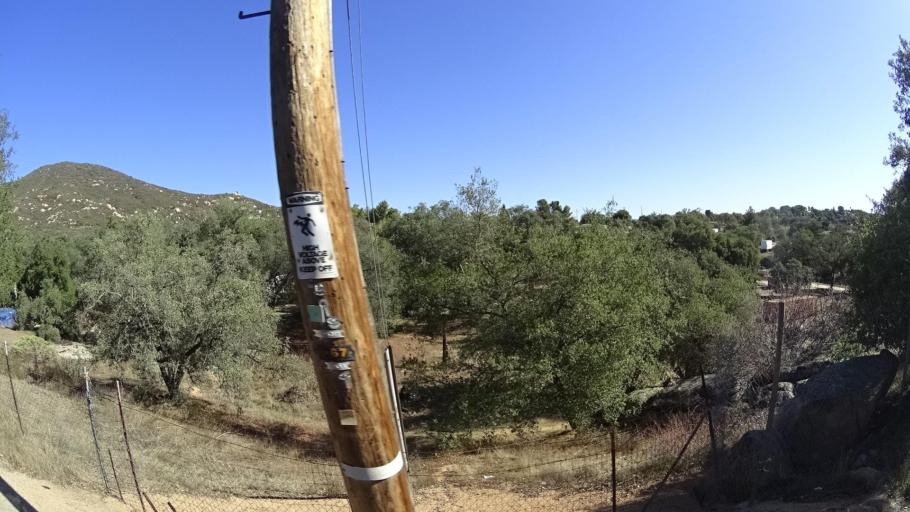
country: MX
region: Baja California
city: Tecate
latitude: 32.6744
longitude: -116.7108
